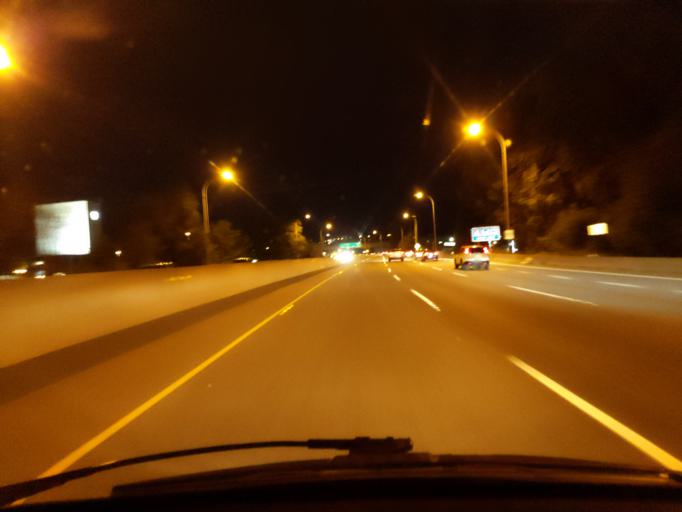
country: CA
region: British Columbia
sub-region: Fraser Valley Regional District
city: North Vancouver
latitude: 49.2660
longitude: -123.0263
